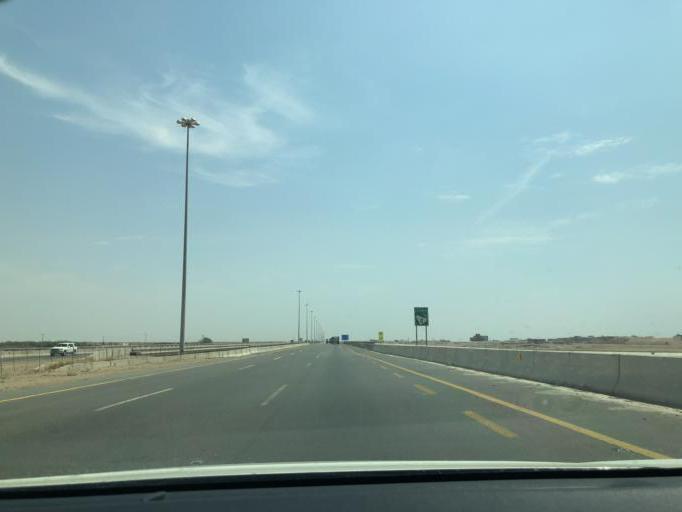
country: SA
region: Makkah
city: Rabigh
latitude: 22.2692
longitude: 39.1234
